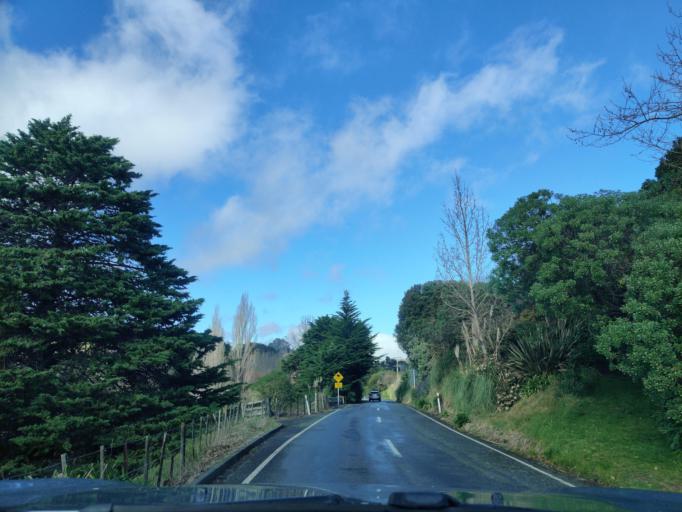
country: NZ
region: Hawke's Bay
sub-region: Hastings District
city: Hastings
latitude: -39.6850
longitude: 176.8985
